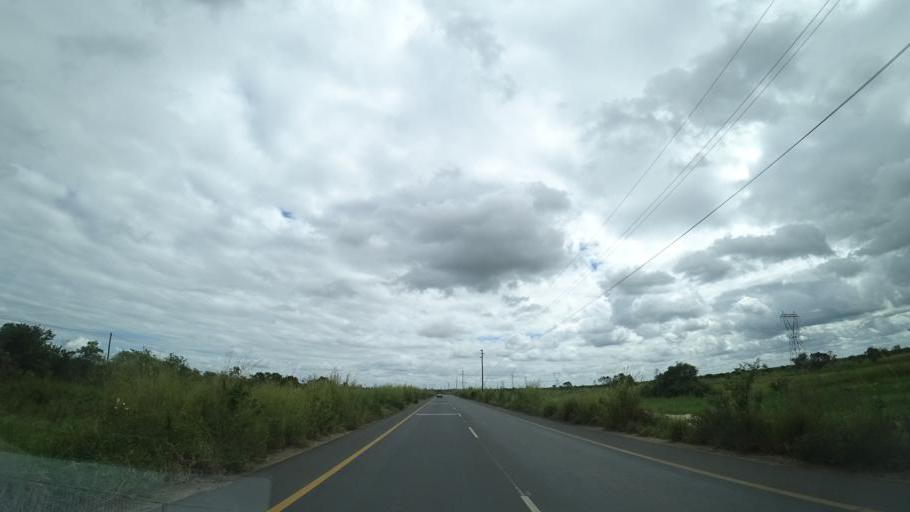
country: MZ
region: Sofala
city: Dondo
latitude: -19.5184
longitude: 34.6205
